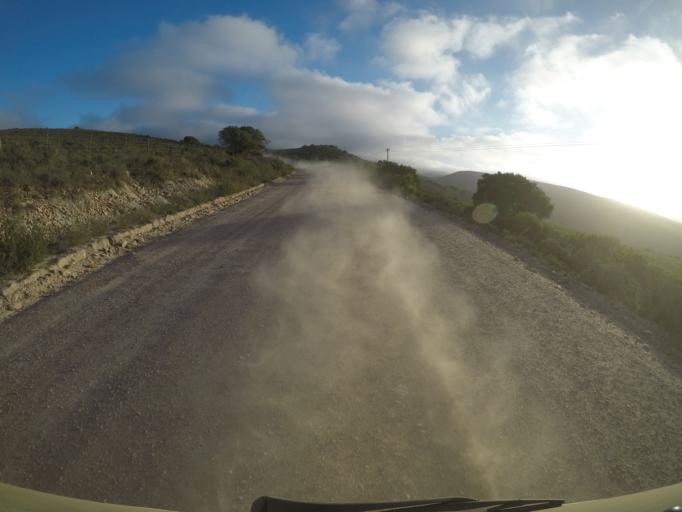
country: ZA
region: Western Cape
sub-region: Eden District Municipality
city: Mossel Bay
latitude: -34.1276
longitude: 22.0488
